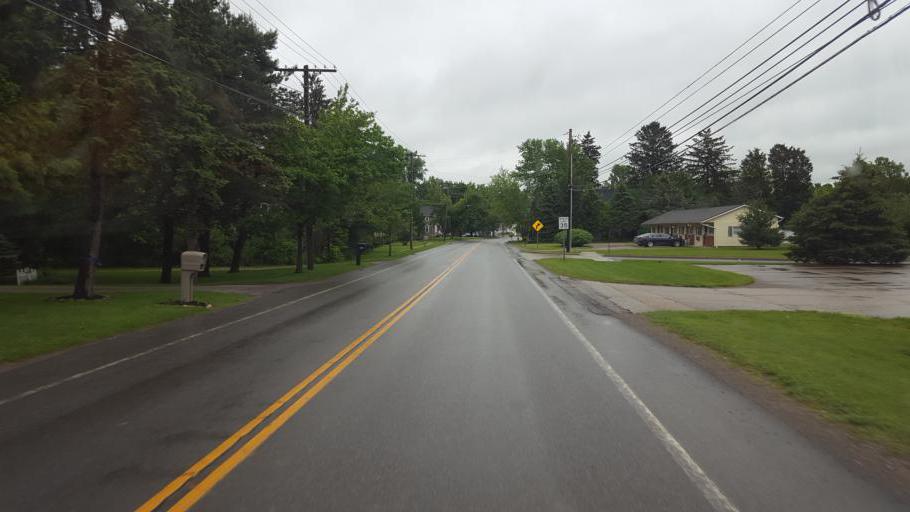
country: US
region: Ohio
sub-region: Medina County
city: Lodi
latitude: 41.0303
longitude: -82.0254
